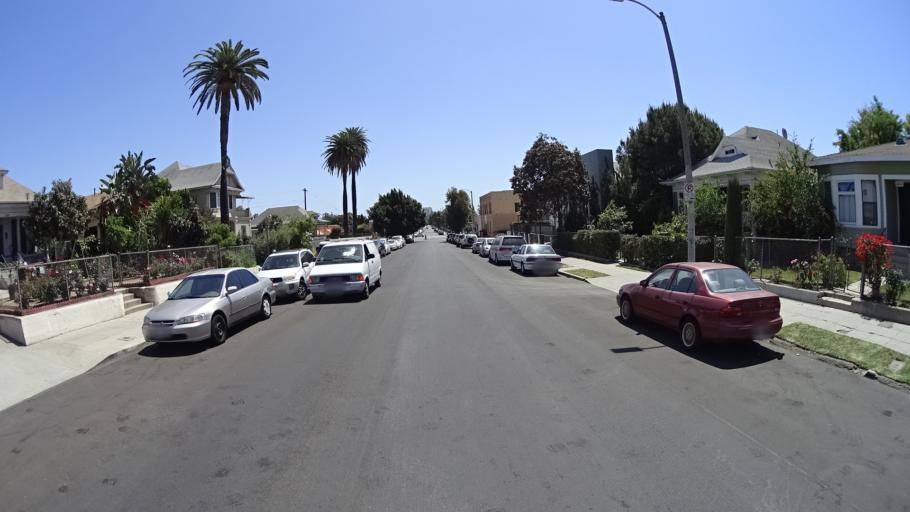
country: US
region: California
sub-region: Los Angeles County
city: Boyle Heights
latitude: 34.0750
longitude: -118.2089
